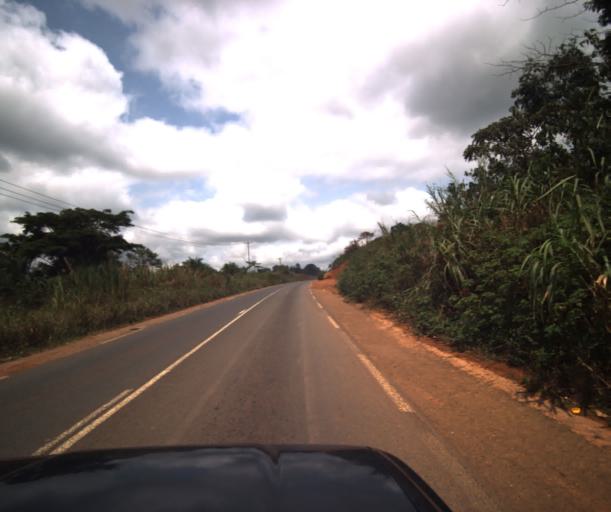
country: CM
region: Centre
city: Mbankomo
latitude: 3.7856
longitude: 11.4501
